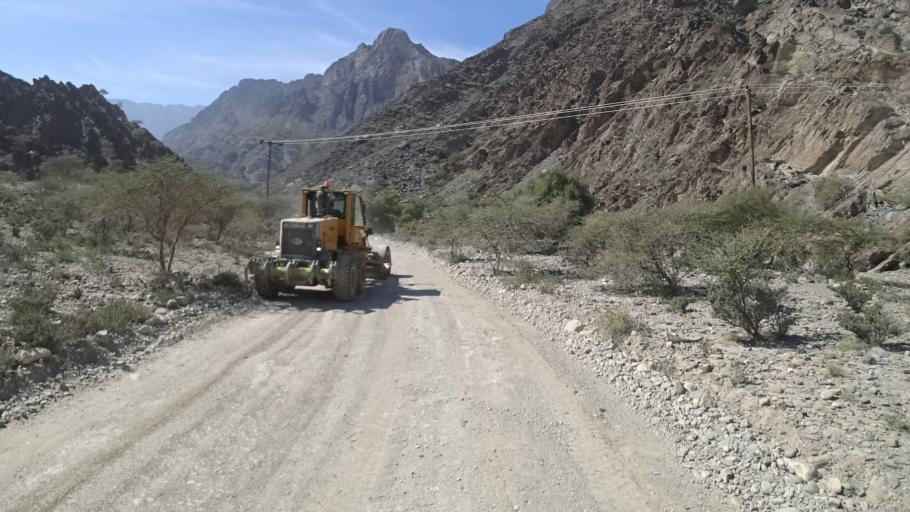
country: OM
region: Al Batinah
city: Bayt al `Awabi
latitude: 23.2236
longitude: 57.4123
